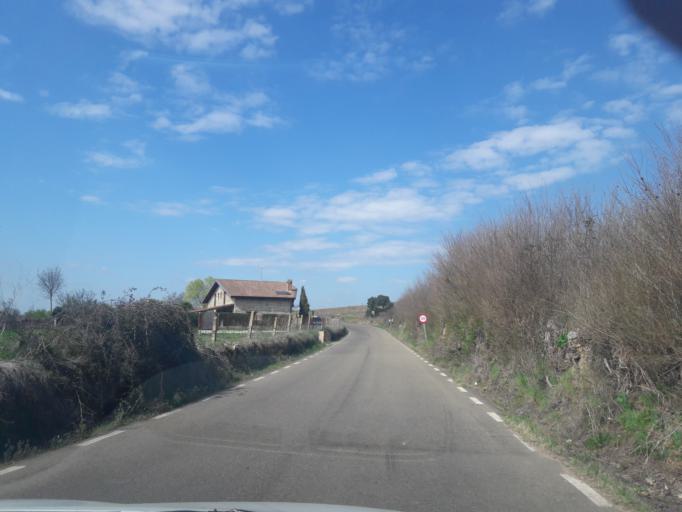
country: ES
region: Castille and Leon
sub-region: Provincia de Salamanca
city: Zamarra
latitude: 40.5676
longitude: -6.4750
